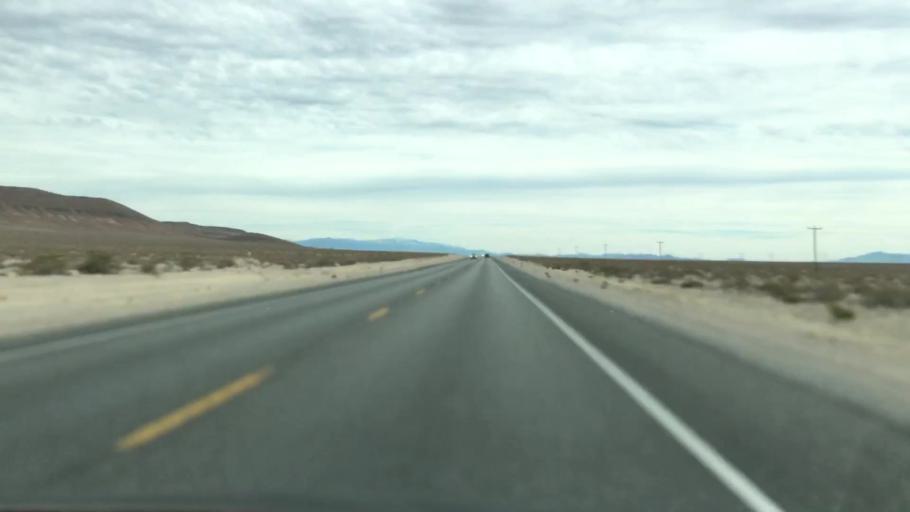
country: US
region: Nevada
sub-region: Nye County
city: Beatty
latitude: 36.7051
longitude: -116.5899
